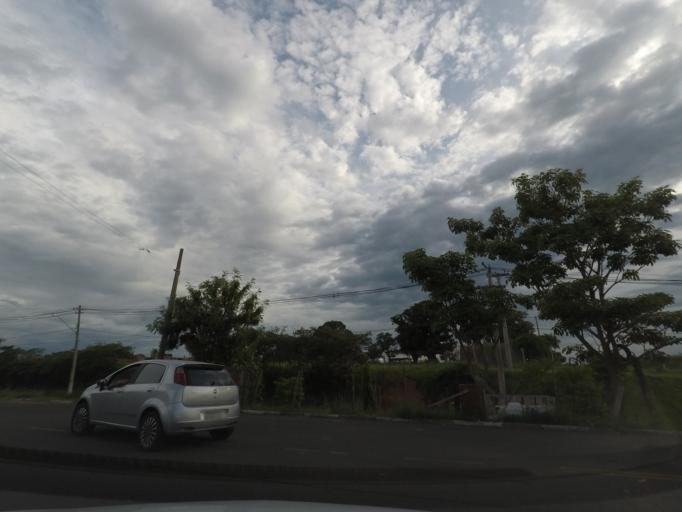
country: BR
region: Sao Paulo
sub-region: Hortolandia
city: Hortolandia
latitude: -22.9545
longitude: -47.2170
